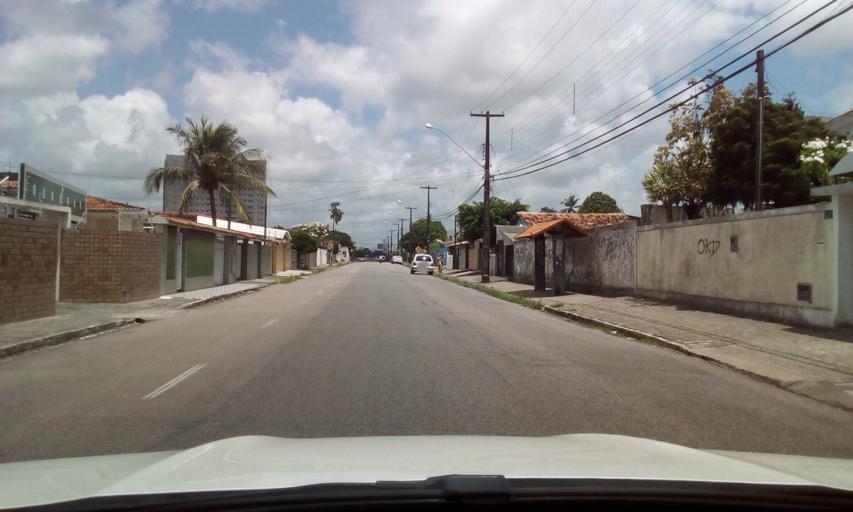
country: BR
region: Paraiba
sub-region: Joao Pessoa
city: Joao Pessoa
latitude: -7.1365
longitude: -34.8758
